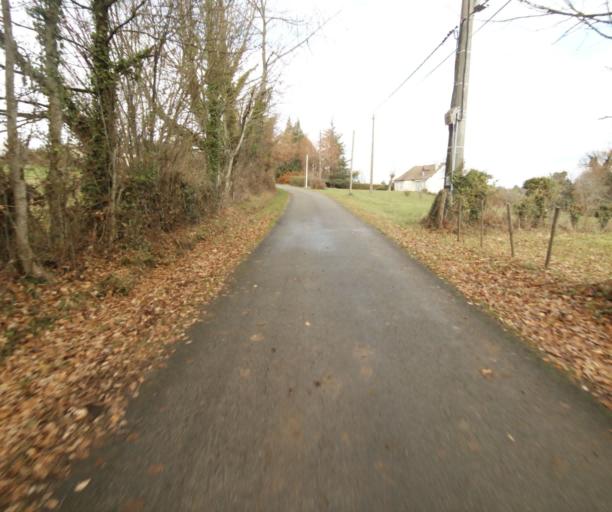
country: FR
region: Limousin
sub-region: Departement de la Correze
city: Sainte-Fereole
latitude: 45.2628
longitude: 1.6035
